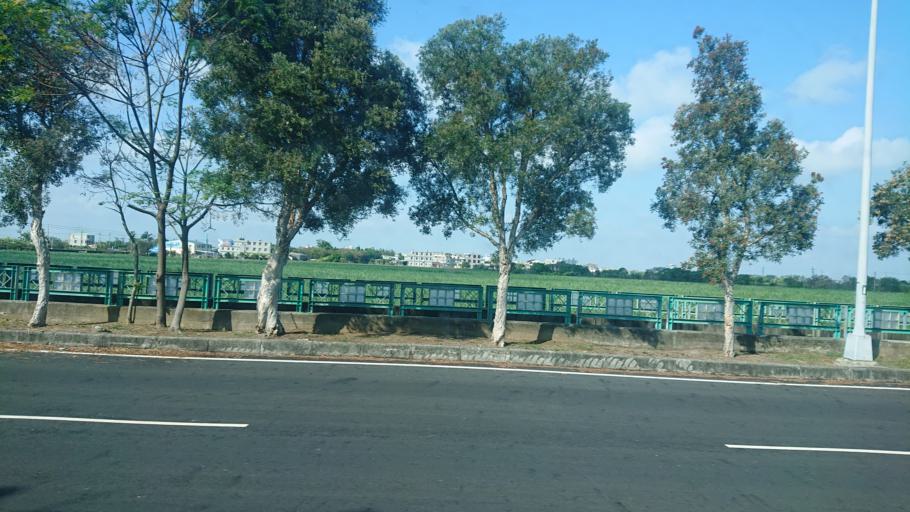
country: TW
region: Taiwan
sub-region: Chiayi
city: Taibao
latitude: 23.4581
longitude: 120.3178
